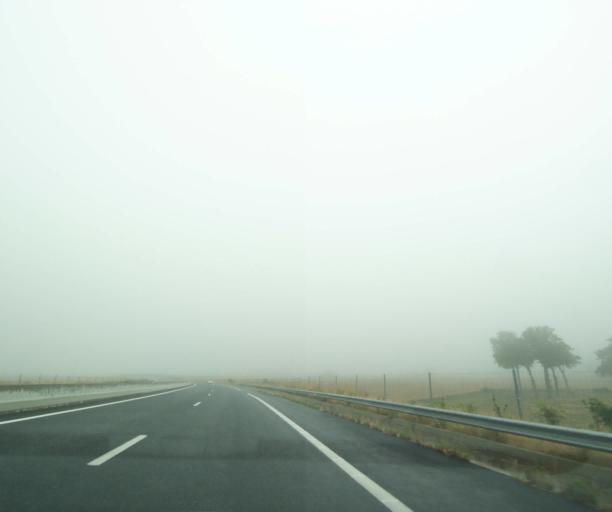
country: FR
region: Midi-Pyrenees
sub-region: Departement de l'Aveyron
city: Naucelle
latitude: 44.1799
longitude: 2.3581
